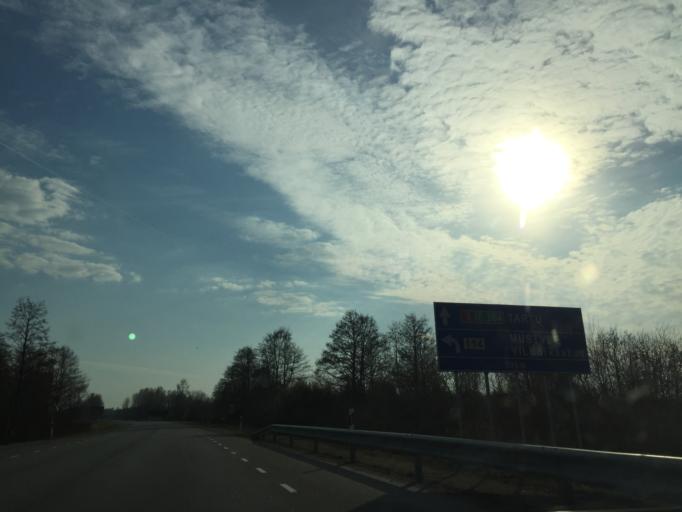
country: EE
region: Jogevamaa
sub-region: Mustvee linn
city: Mustvee
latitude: 58.8912
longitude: 26.9682
